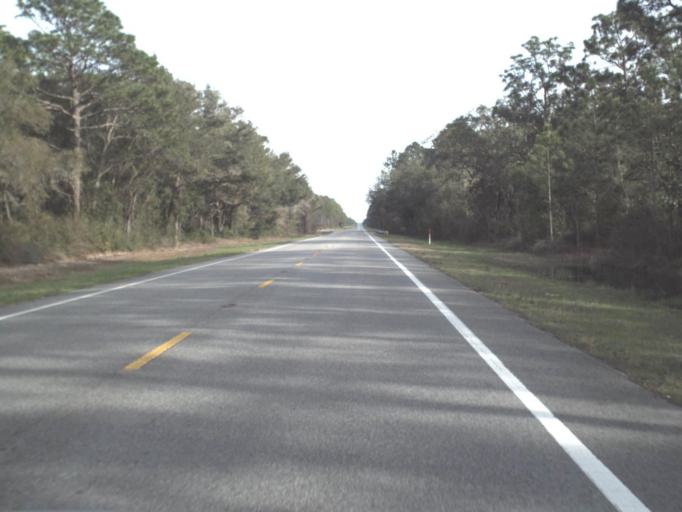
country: US
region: Florida
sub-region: Bay County
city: Mexico Beach
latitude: 29.9724
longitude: -85.4601
